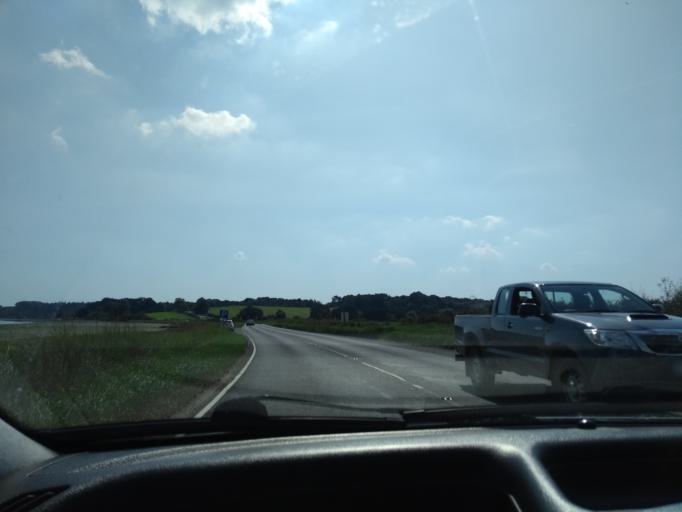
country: GB
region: England
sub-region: Suffolk
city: Ipswich
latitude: 52.0220
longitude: 1.1640
